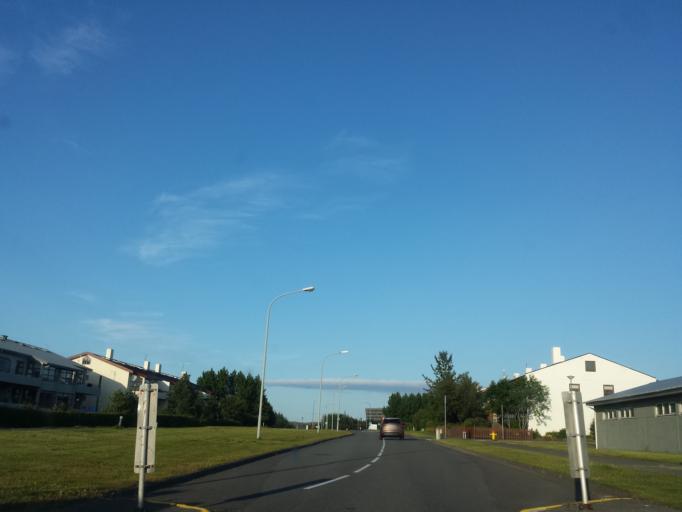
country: IS
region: Capital Region
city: Reykjavik
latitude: 64.1212
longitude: -21.8172
